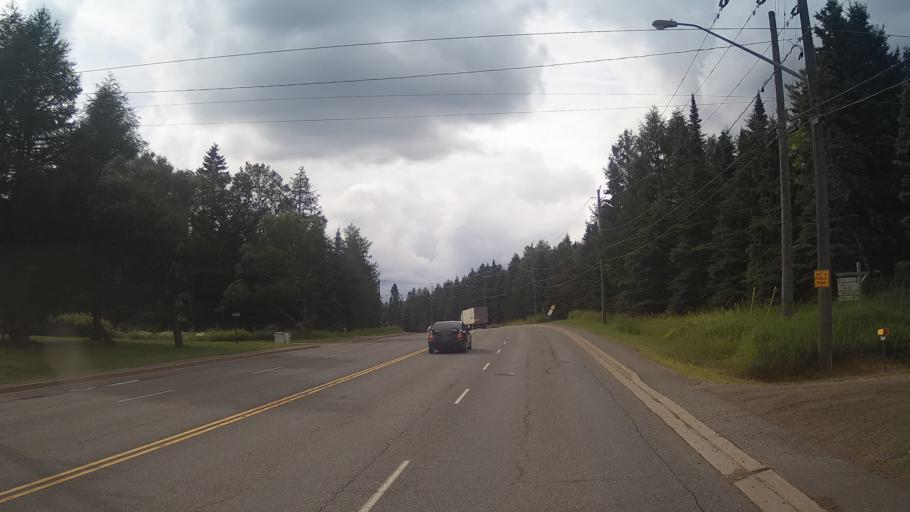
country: CA
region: Ontario
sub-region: Thunder Bay District
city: Thunder Bay
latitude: 48.4588
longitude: -89.2681
